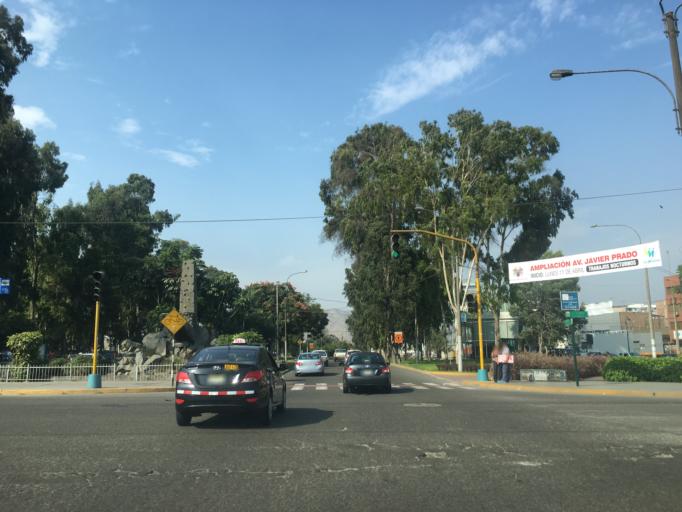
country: PE
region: Lima
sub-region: Lima
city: La Molina
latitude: -12.0717
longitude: -76.9567
